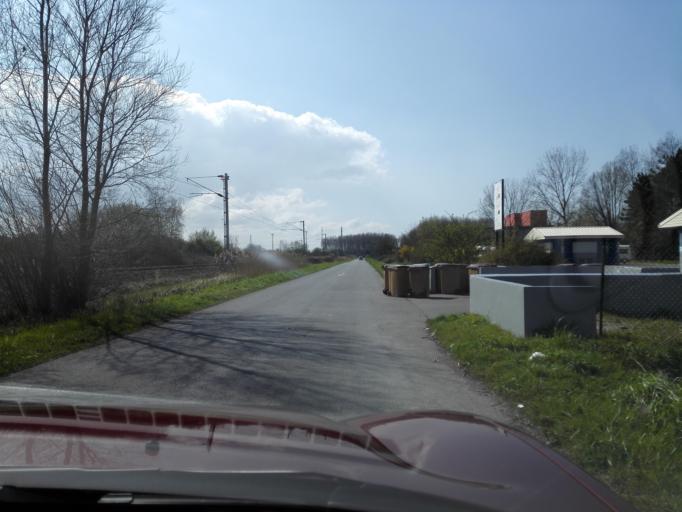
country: FR
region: Nord-Pas-de-Calais
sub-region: Departement du Nord
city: Grande-Synthe
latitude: 51.0020
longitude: 2.3045
